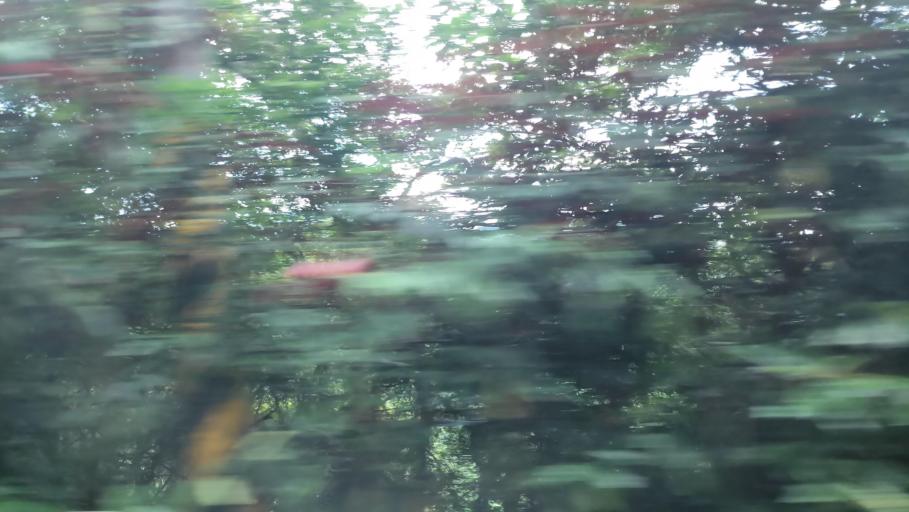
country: TW
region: Taipei
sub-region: Taipei
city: Banqiao
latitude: 24.8895
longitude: 121.4259
